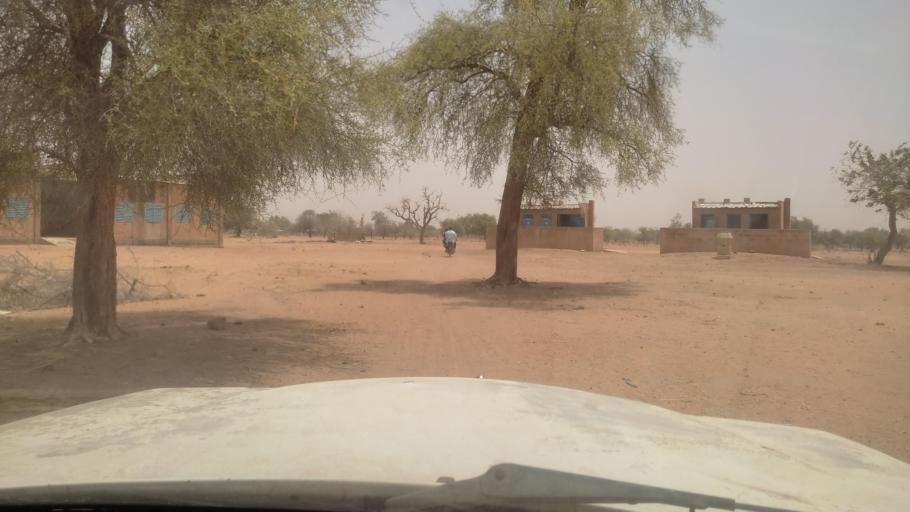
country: BF
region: Est
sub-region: Gnagna Province
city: Bogande
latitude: 13.0046
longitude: -0.0930
